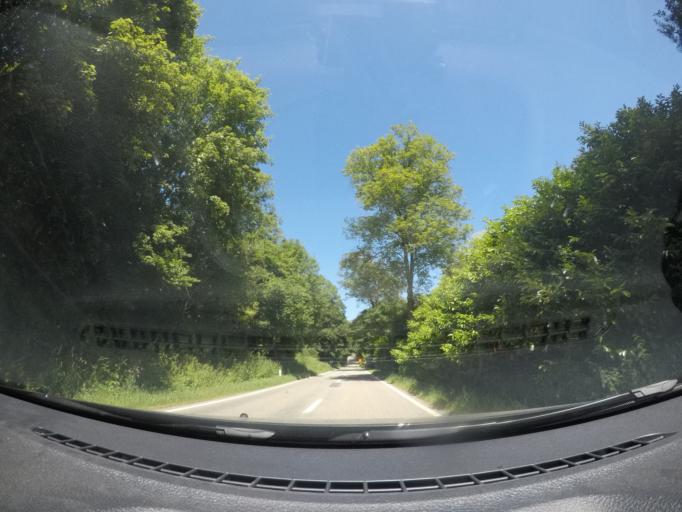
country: BE
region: Wallonia
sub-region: Province du Luxembourg
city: Wellin
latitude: 50.0680
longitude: 5.1385
